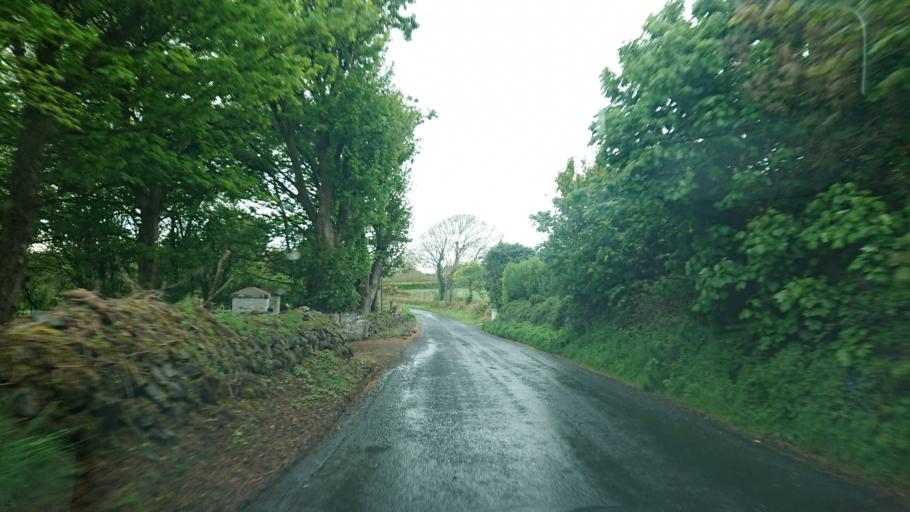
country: IE
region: Munster
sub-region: Waterford
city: Waterford
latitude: 52.2294
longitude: -7.0729
